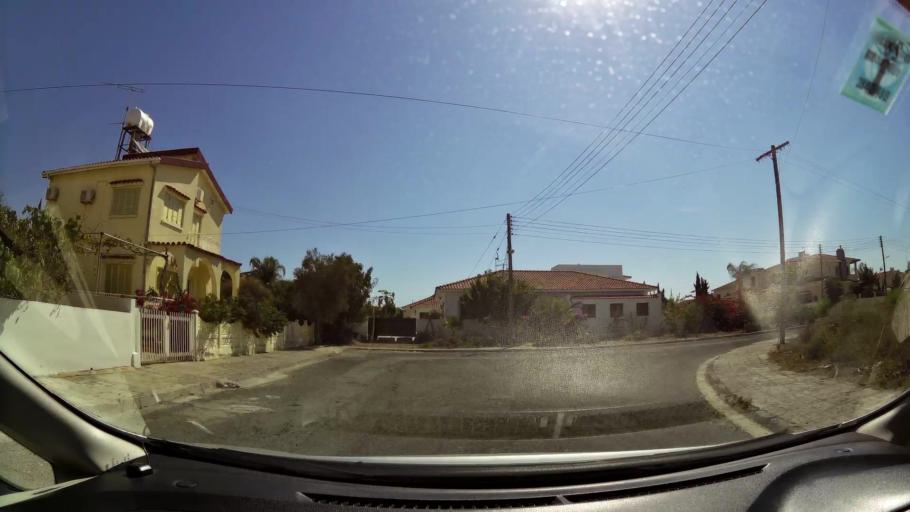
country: CY
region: Larnaka
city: Voroklini
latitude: 34.9620
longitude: 33.6550
